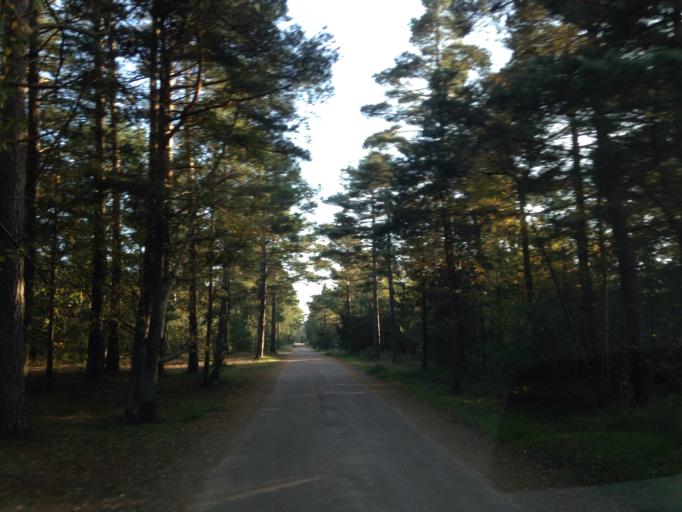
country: SE
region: Skane
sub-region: Vellinge Kommun
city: Ljunghusen
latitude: 55.4016
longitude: 12.9265
